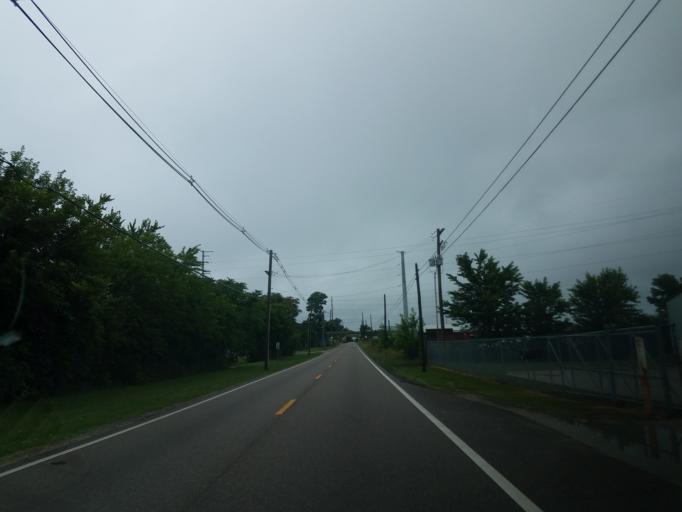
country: US
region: Illinois
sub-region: McLean County
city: Bloomington
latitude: 40.4558
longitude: -88.9814
